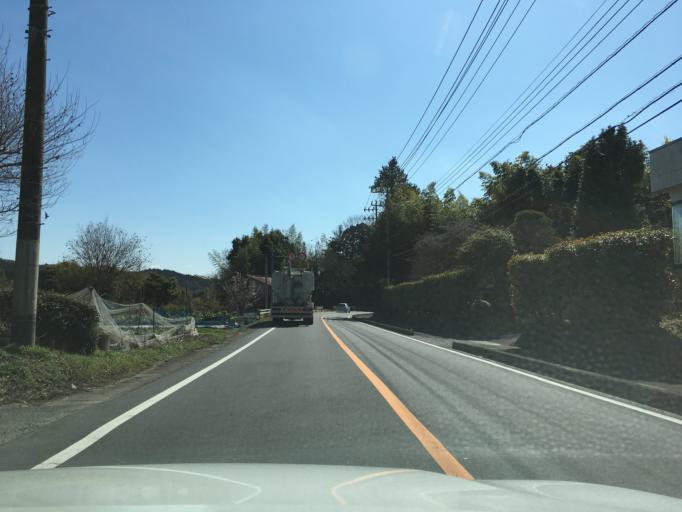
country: JP
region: Tochigi
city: Otawara
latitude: 36.8882
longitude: 140.1184
